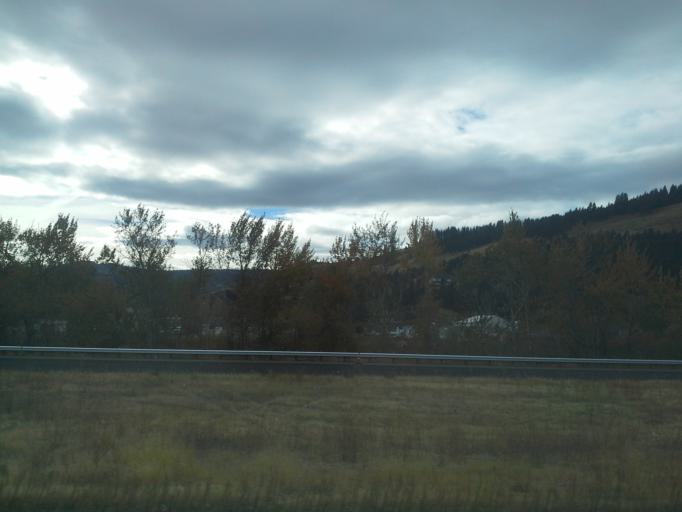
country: US
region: Oregon
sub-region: Union County
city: La Grande
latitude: 45.3442
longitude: -118.1085
